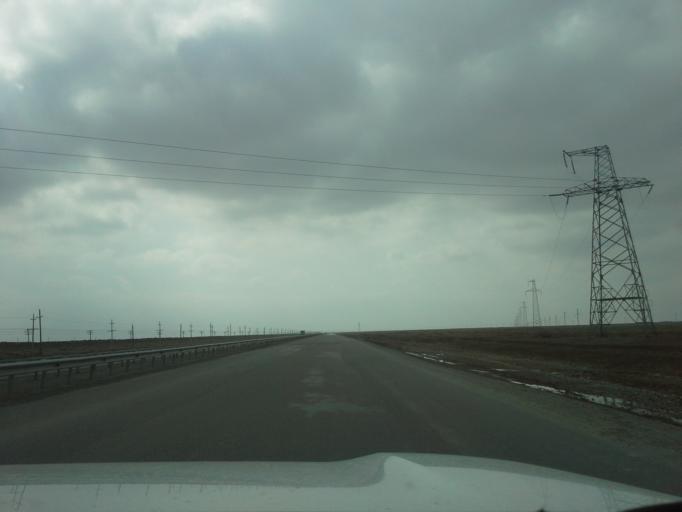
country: IR
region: Razavi Khorasan
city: Kalat-e Naderi
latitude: 37.2148
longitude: 60.0905
